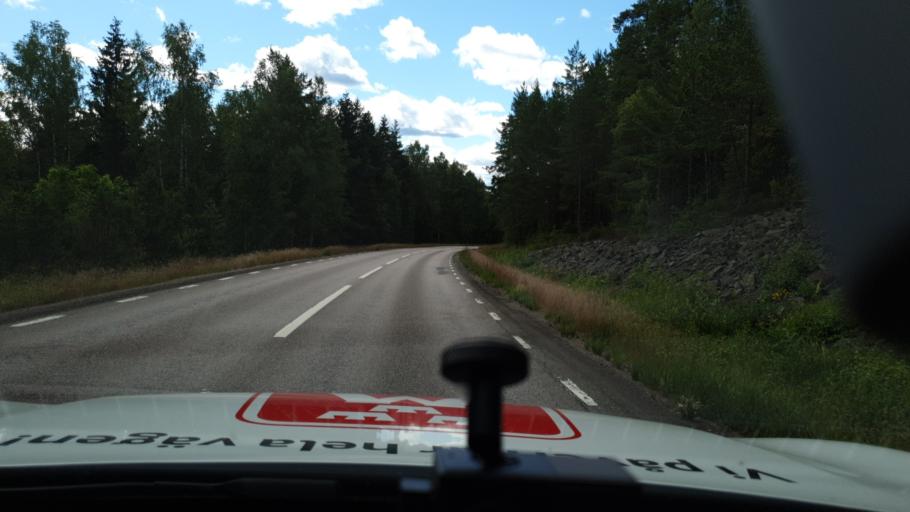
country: SE
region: Vaermland
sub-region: Sunne Kommun
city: Sunne
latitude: 59.6826
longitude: 13.0470
